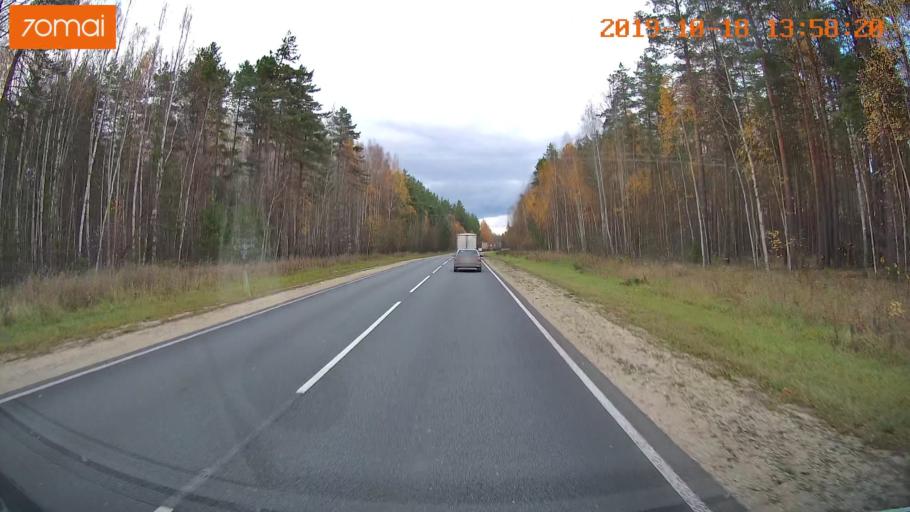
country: RU
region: Rjazan
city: Spas-Klepiki
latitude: 55.0837
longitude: 40.0534
